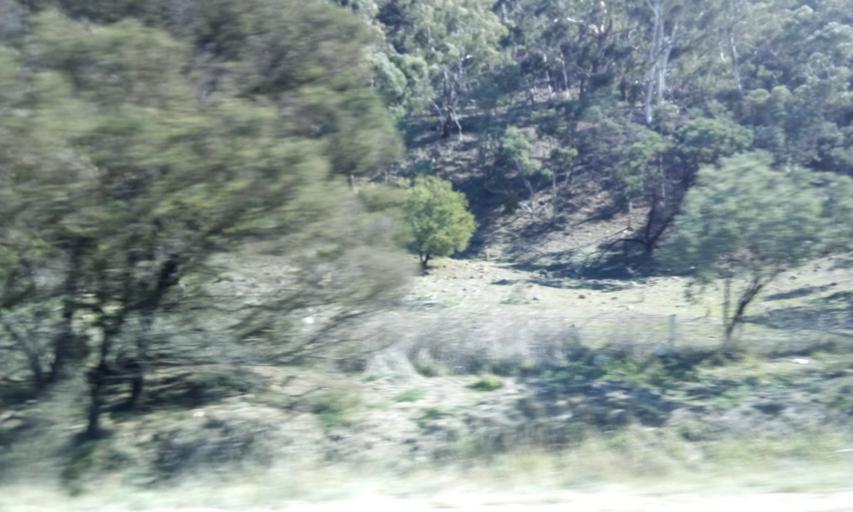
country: AU
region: New South Wales
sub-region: Yass Valley
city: Gundaroo
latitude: -35.0464
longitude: 149.3763
